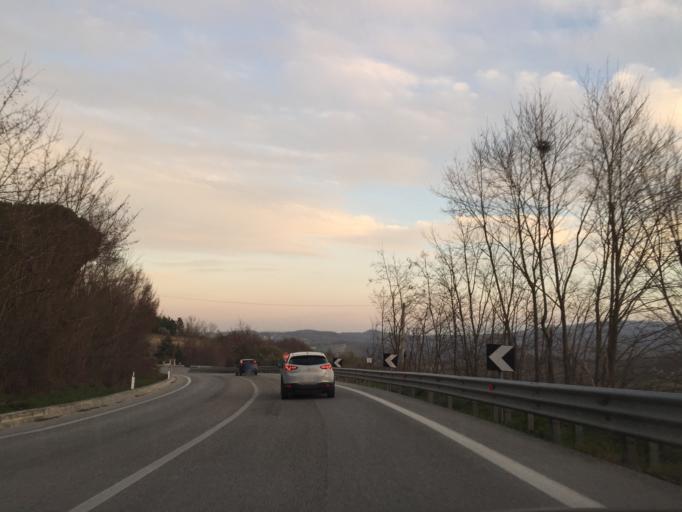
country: IT
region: Molise
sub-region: Provincia di Campobasso
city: Campodipietra
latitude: 41.5557
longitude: 14.7315
